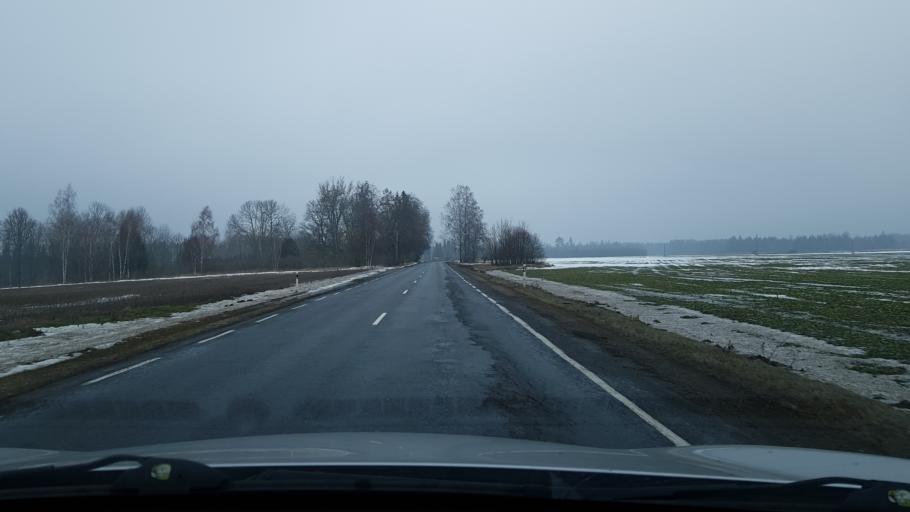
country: EE
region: Valgamaa
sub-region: Torva linn
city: Torva
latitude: 58.1567
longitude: 25.9637
